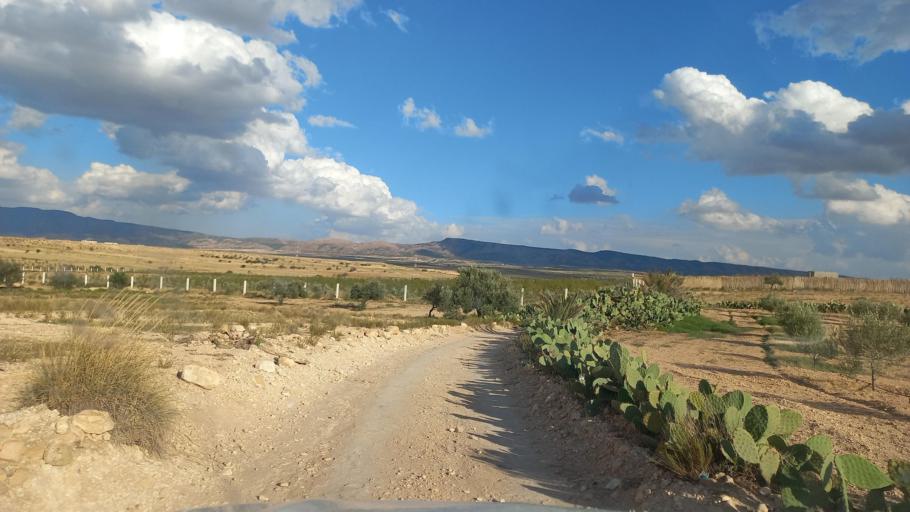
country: TN
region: Al Qasrayn
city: Sbiba
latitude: 35.3797
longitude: 9.0750
